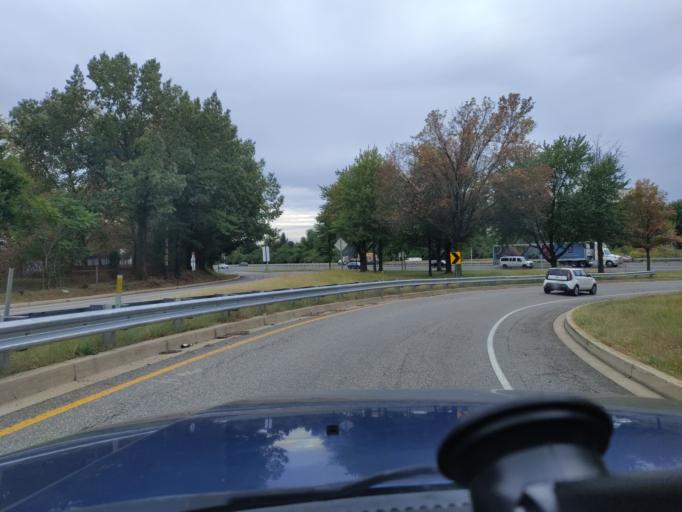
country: US
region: Maryland
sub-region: Frederick County
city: Frederick
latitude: 39.4059
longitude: -77.4312
